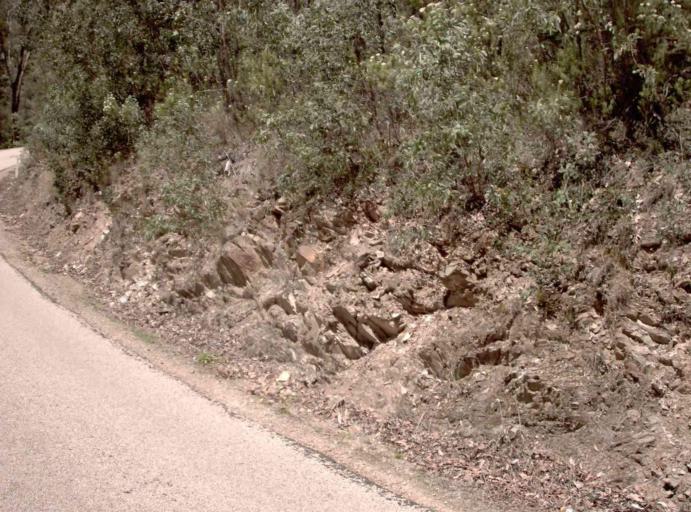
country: AU
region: Victoria
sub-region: East Gippsland
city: Bairnsdale
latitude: -37.4563
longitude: 147.8329
